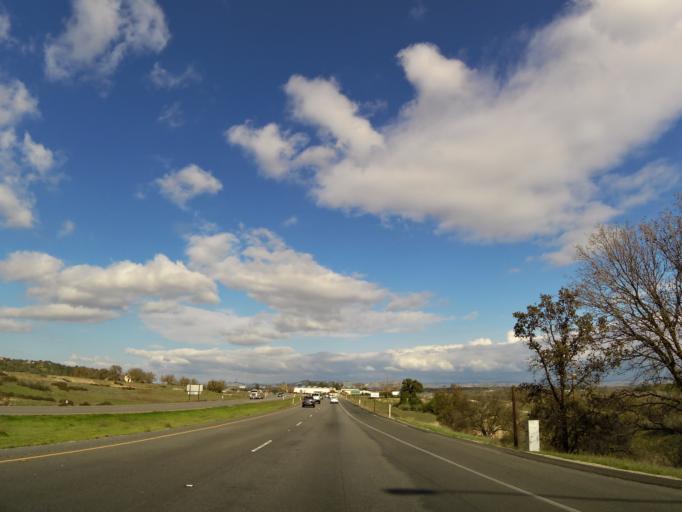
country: US
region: California
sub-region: San Luis Obispo County
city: Paso Robles
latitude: 35.6643
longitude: -120.6966
